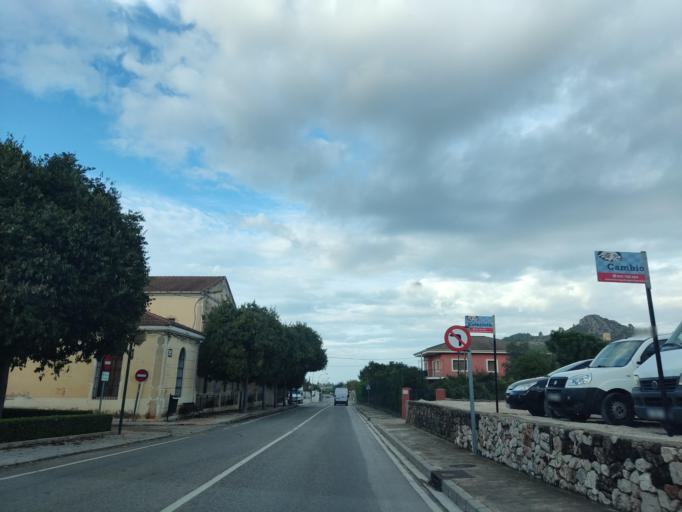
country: ES
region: Valencia
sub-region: Provincia de Alicante
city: Pedreguer
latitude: 38.7975
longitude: 0.0324
